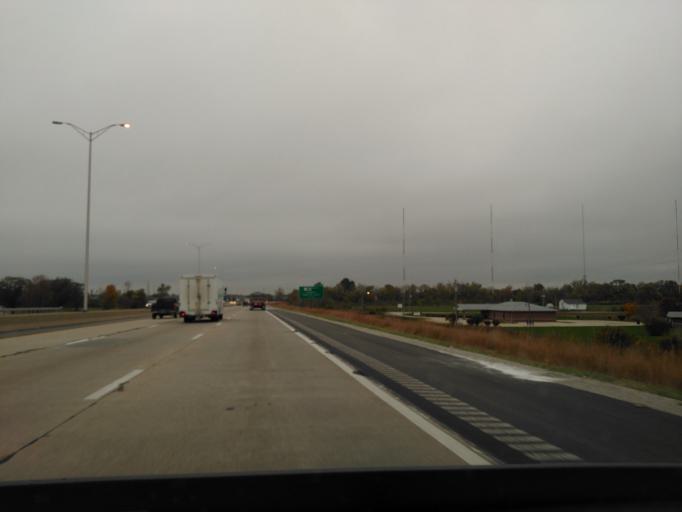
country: US
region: Illinois
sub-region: Saint Clair County
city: Dupo
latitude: 38.5364
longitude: -90.1868
